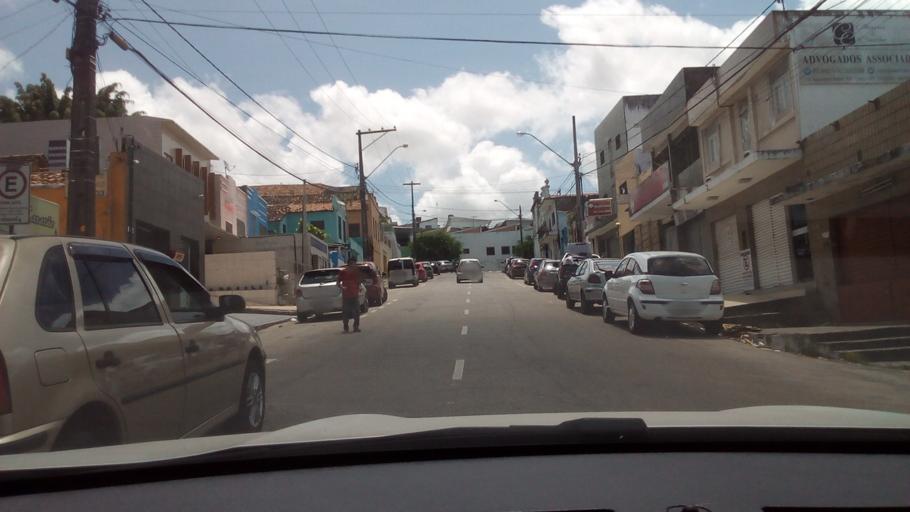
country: BR
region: Paraiba
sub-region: Joao Pessoa
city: Joao Pessoa
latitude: -7.1221
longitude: -34.8875
